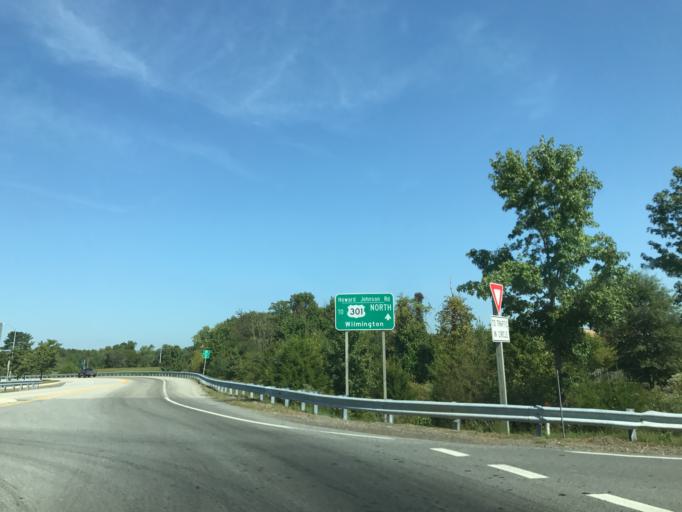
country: US
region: Maryland
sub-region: Queen Anne's County
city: Kingstown
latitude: 39.2638
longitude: -75.8625
